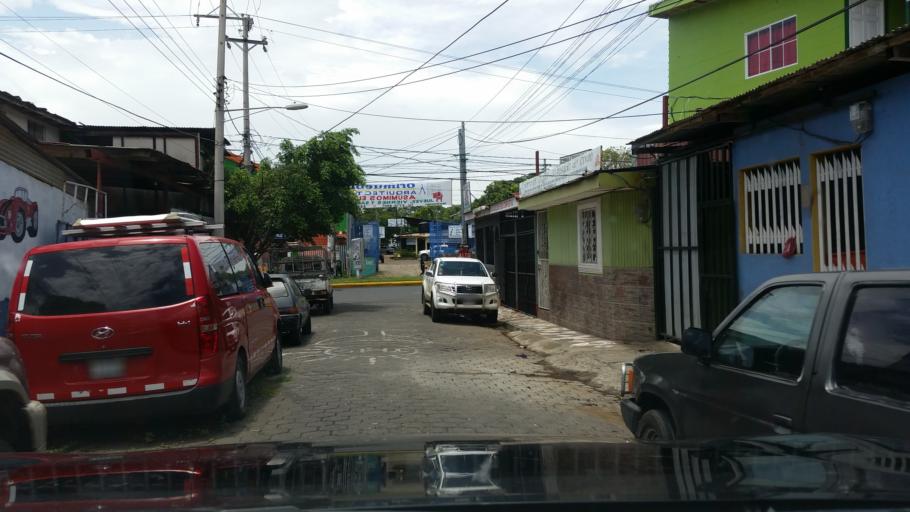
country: NI
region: Managua
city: Managua
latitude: 12.1305
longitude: -86.2572
